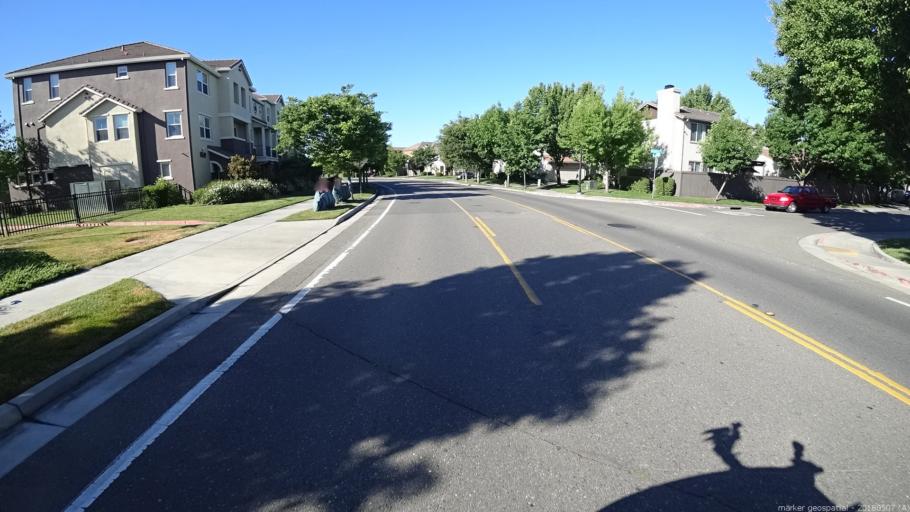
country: US
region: California
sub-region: Sacramento County
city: Elverta
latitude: 38.6730
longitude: -121.5039
